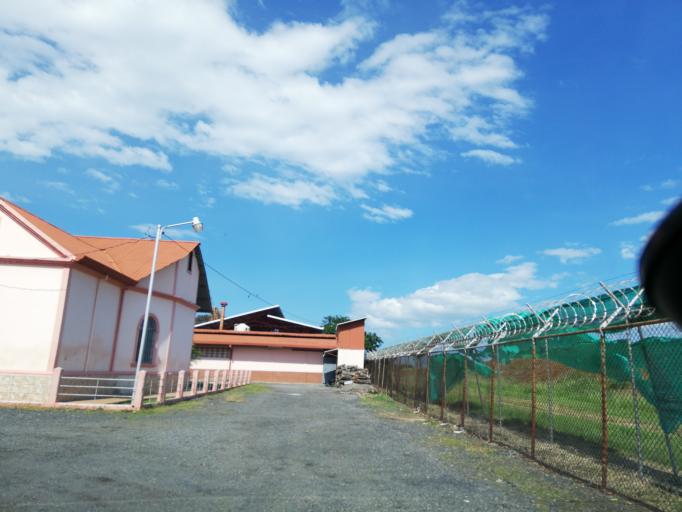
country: CR
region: Alajuela
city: Alajuela
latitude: 9.9874
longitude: -84.2192
